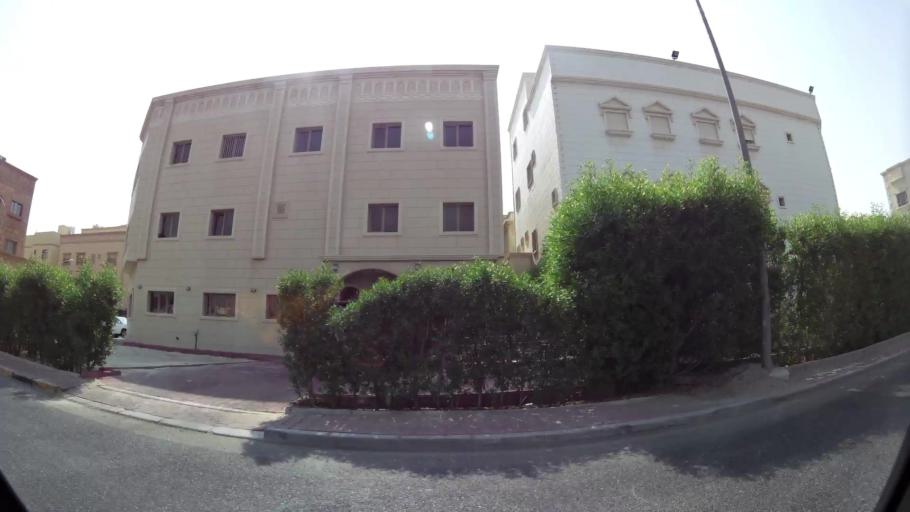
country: KW
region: Muhafazat al Jahra'
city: Al Jahra'
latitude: 29.3040
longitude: 47.7008
